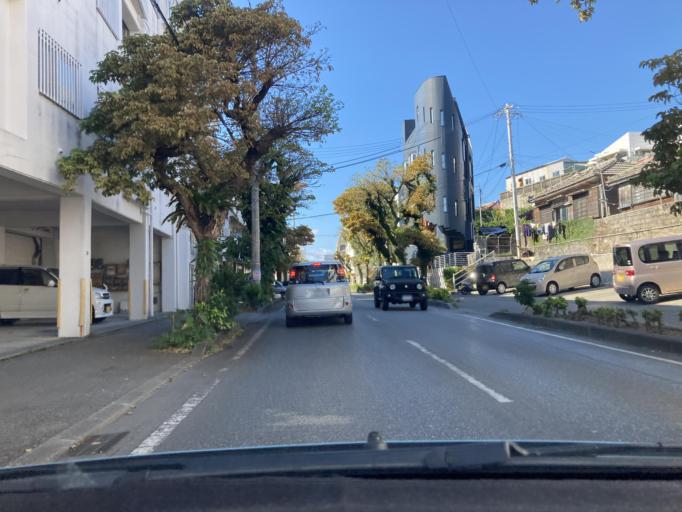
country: JP
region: Okinawa
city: Naha-shi
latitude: 26.2399
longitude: 127.6966
